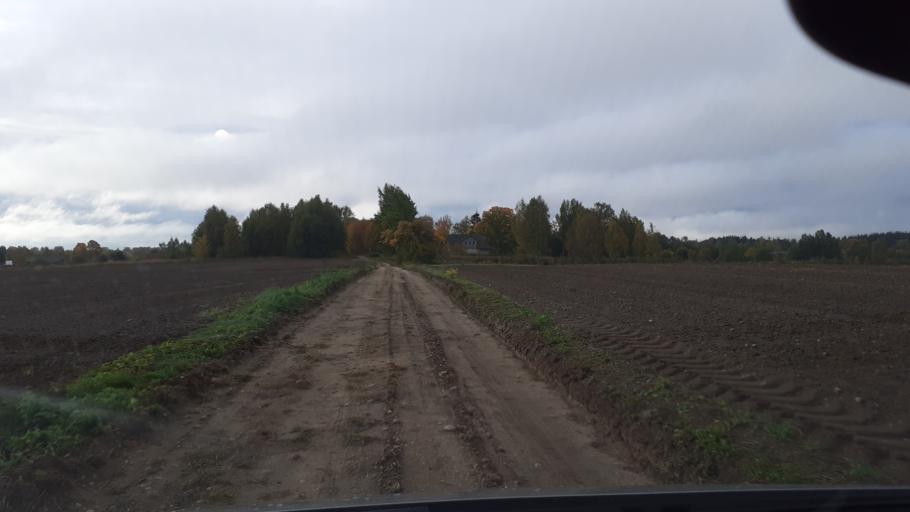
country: LV
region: Kuldigas Rajons
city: Kuldiga
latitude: 56.9756
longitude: 21.9395
